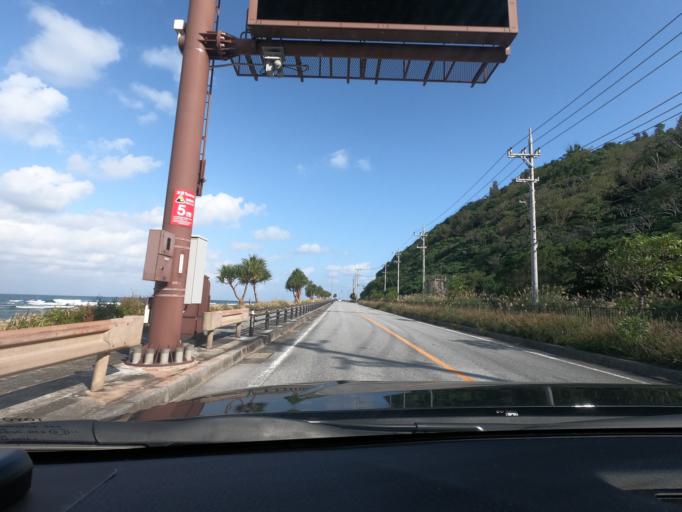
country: JP
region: Okinawa
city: Nago
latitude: 26.7583
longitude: 128.1892
